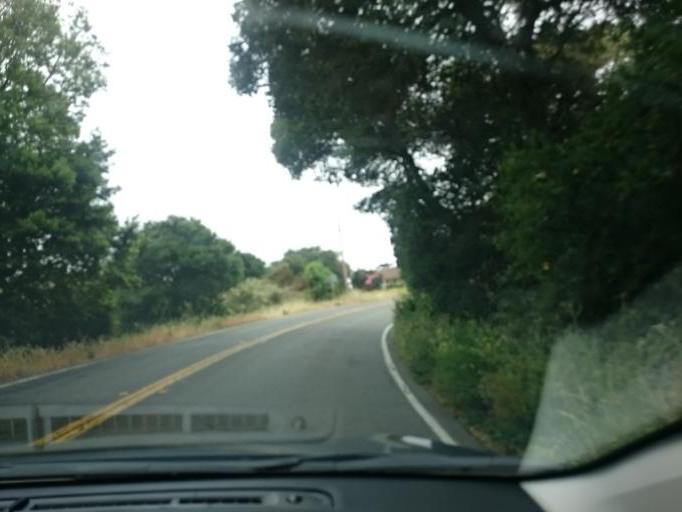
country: US
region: California
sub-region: Marin County
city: Lagunitas-Forest Knolls
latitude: 38.0249
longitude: -122.7757
